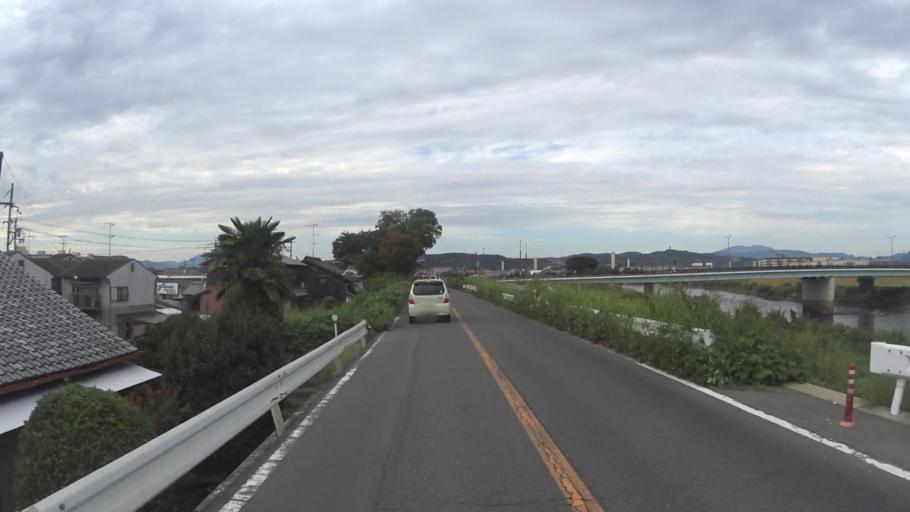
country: JP
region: Kyoto
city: Uji
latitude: 34.9146
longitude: 135.7890
